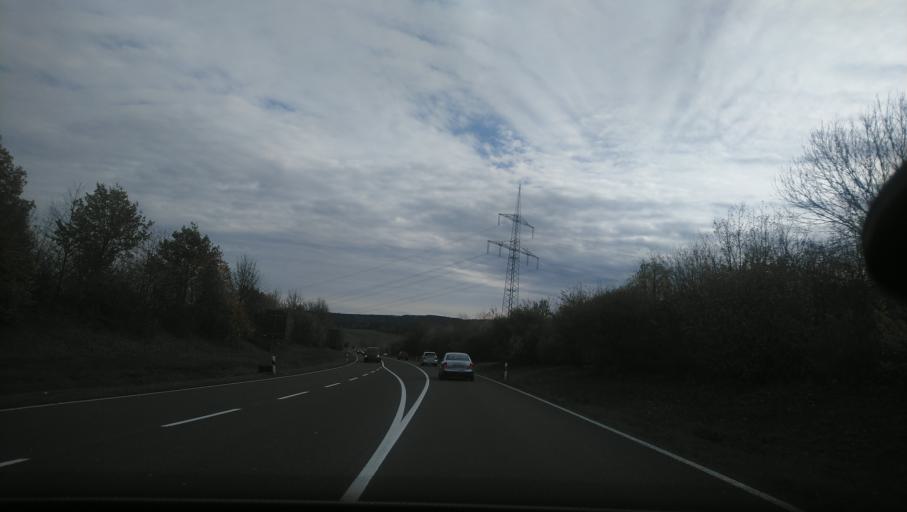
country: DE
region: Saxony
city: Zwonitz
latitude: 50.6519
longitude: 12.8155
